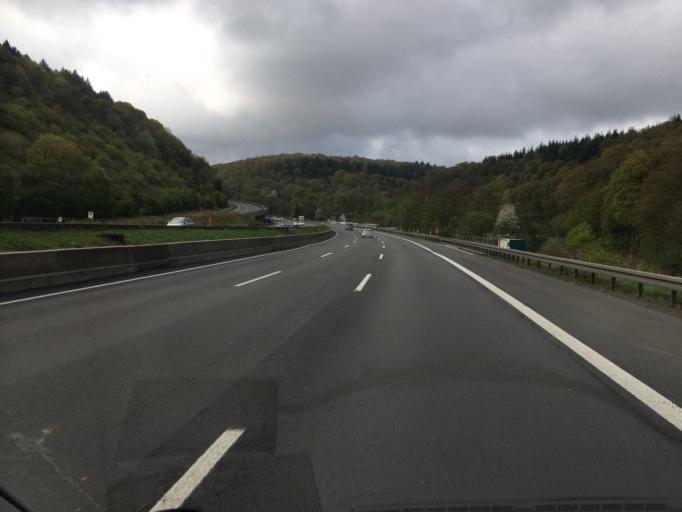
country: DE
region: North Rhine-Westphalia
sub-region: Regierungsbezirk Dusseldorf
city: Wuppertal
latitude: 51.2538
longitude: 7.2265
